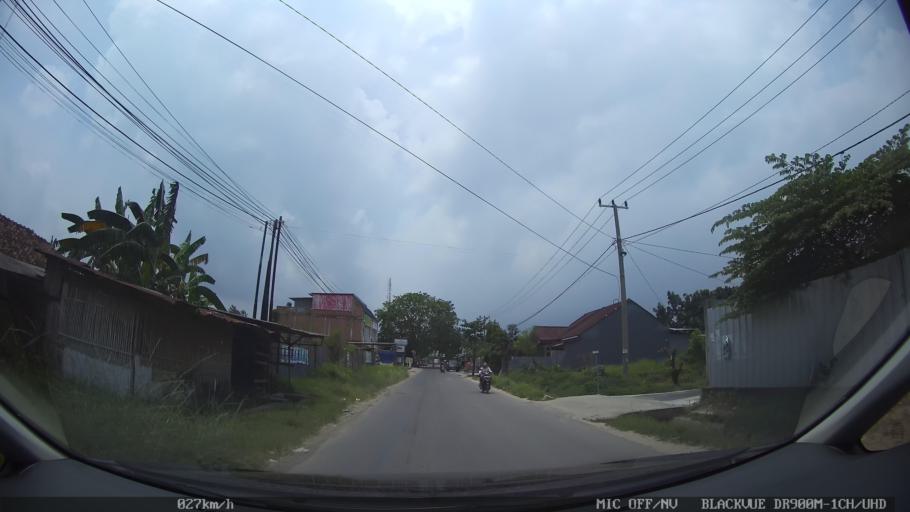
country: ID
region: Lampung
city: Kedaton
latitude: -5.3944
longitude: 105.3044
